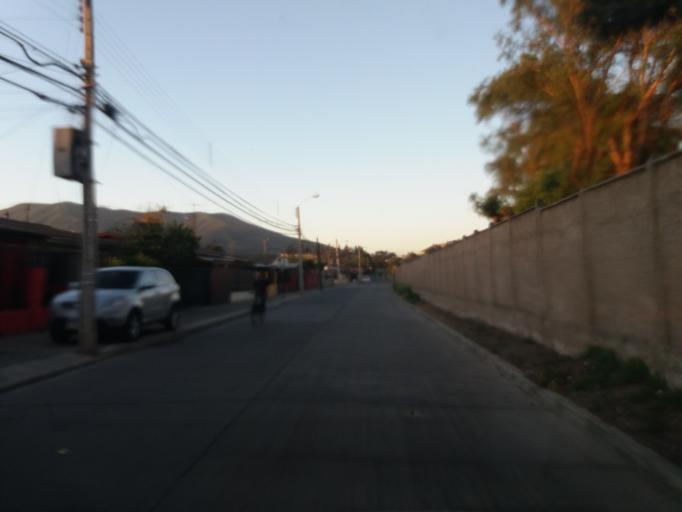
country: CL
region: Valparaiso
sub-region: Provincia de Quillota
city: Quillota
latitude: -32.8830
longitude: -71.2552
